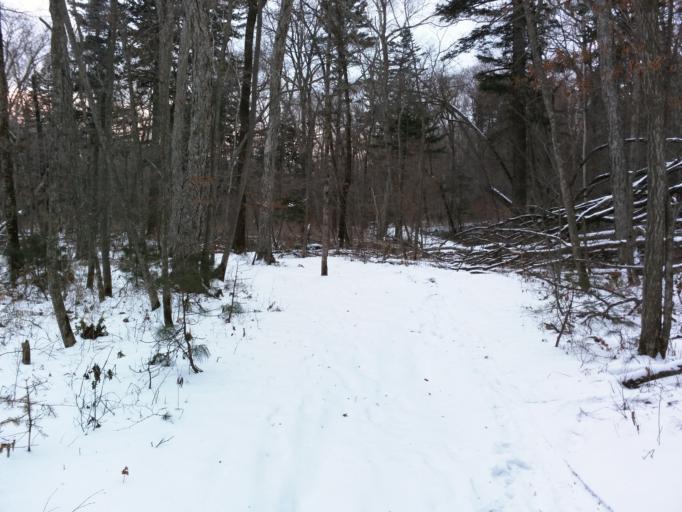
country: RU
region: Primorskiy
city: Trudovoye
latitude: 43.2014
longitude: 132.0291
